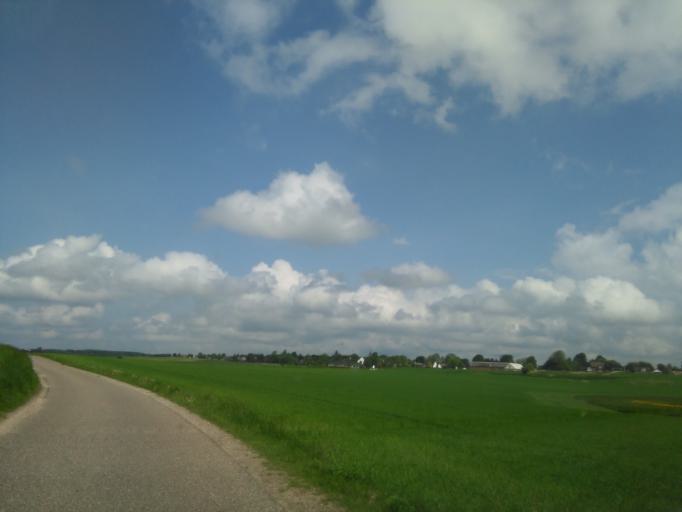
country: DK
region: Central Jutland
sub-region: Arhus Kommune
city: Sabro
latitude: 56.2151
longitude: 9.9801
